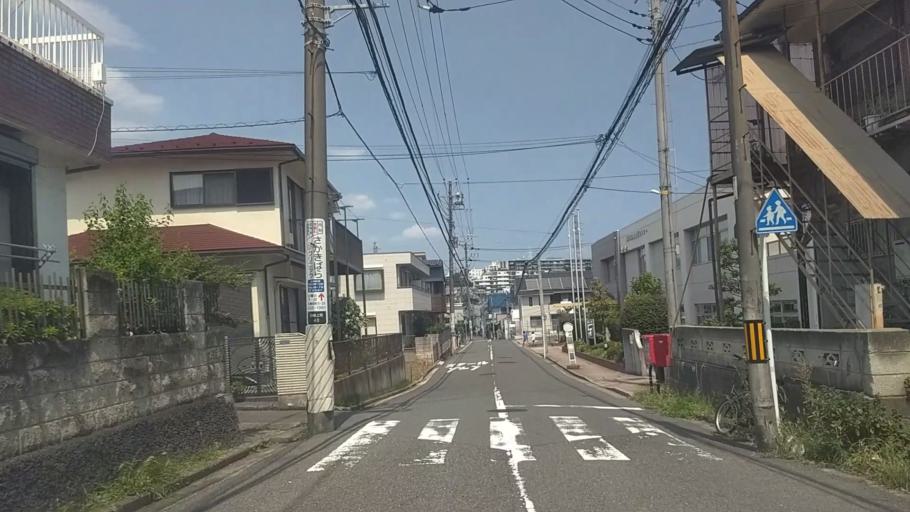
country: JP
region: Kanagawa
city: Yokohama
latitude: 35.4892
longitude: 139.6321
